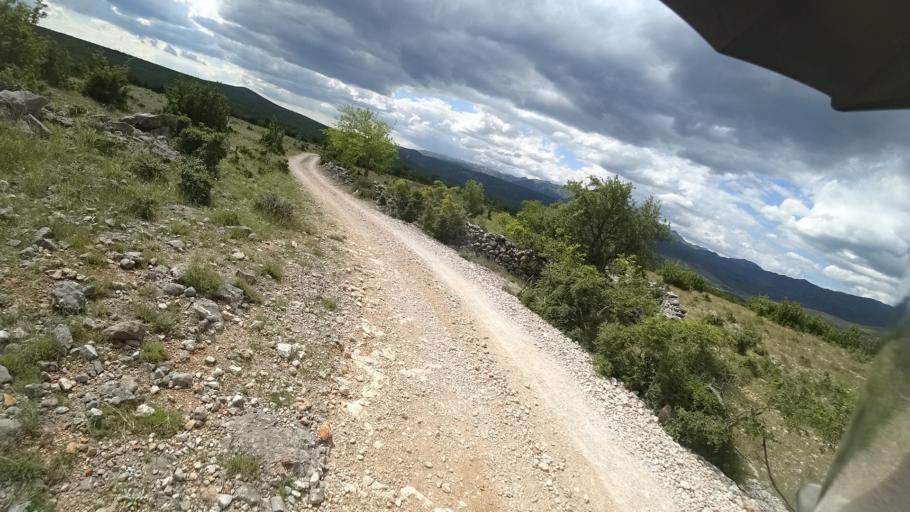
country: HR
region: Zadarska
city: Gracac
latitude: 44.1760
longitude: 15.9186
